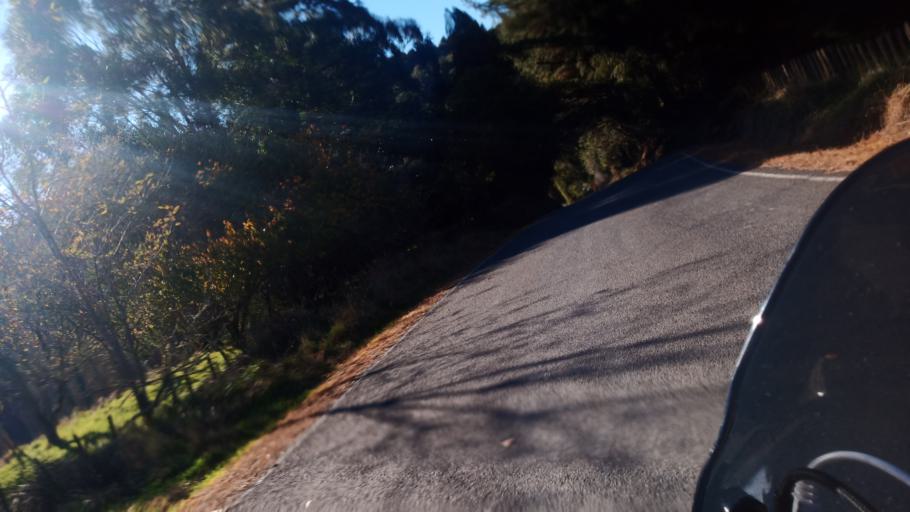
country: NZ
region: Hawke's Bay
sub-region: Wairoa District
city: Wairoa
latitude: -38.8183
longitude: 177.2959
